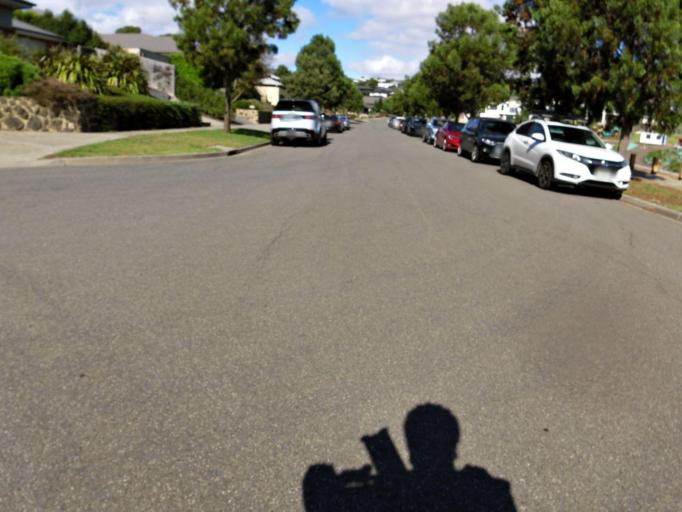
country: AU
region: Victoria
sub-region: Greater Geelong
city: Wandana Heights
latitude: -38.1594
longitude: 144.3027
